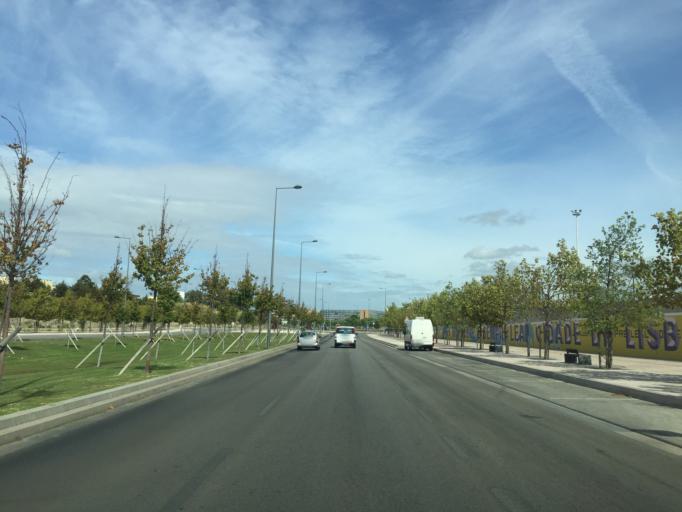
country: PT
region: Lisbon
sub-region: Odivelas
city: Olival do Basto
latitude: 38.7707
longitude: -9.1488
